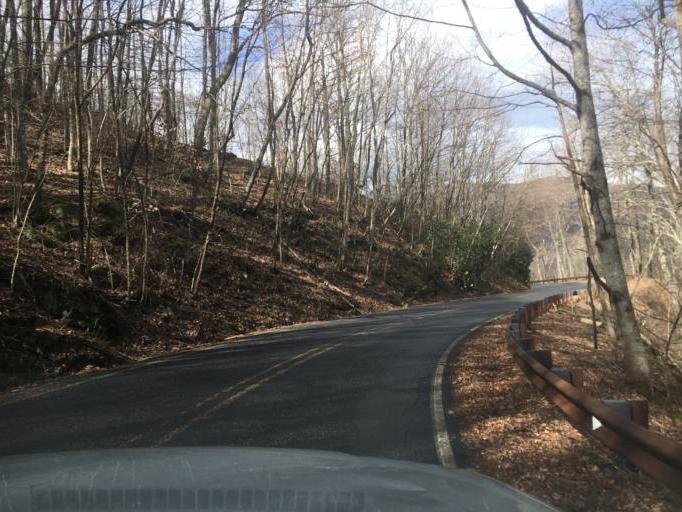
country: US
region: North Carolina
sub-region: Transylvania County
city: Brevard
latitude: 35.3706
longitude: -82.8064
